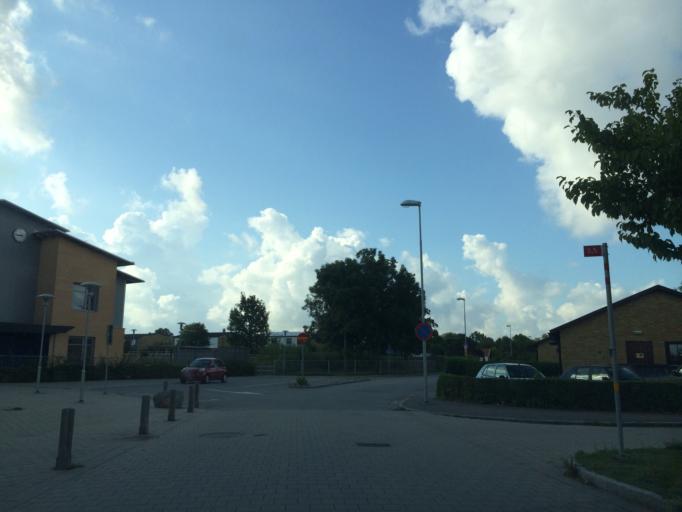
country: SE
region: Skane
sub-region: Lomma Kommun
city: Lomma
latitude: 55.6713
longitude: 13.0795
